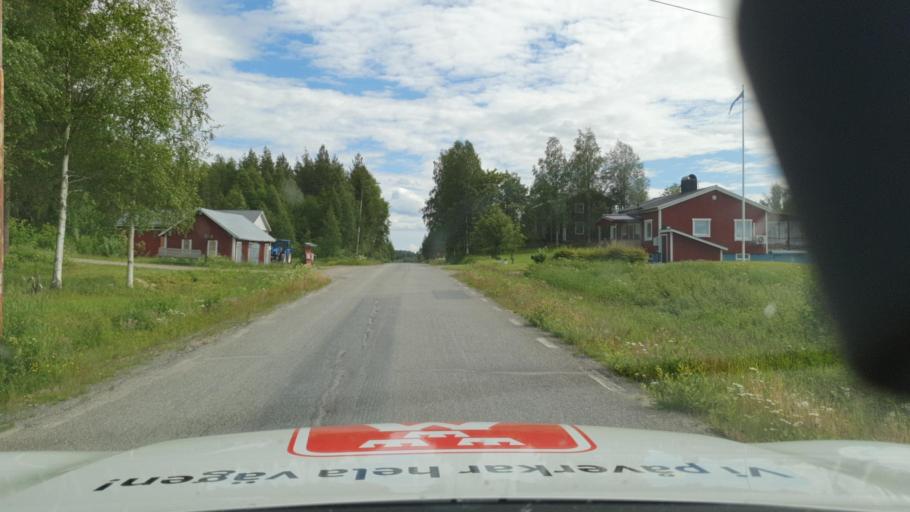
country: SE
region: Vaesterbotten
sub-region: Norsjo Kommun
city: Norsjoe
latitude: 64.8765
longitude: 19.4689
